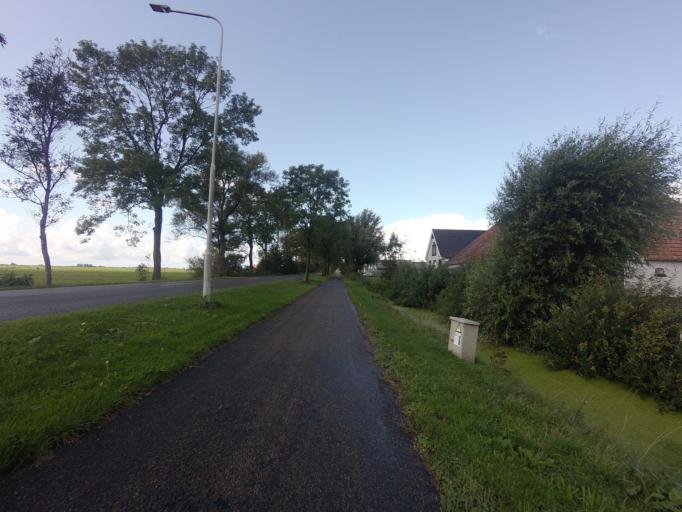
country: NL
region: Friesland
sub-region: Gemeente Boarnsterhim
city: Warten
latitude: 53.1497
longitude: 5.8834
